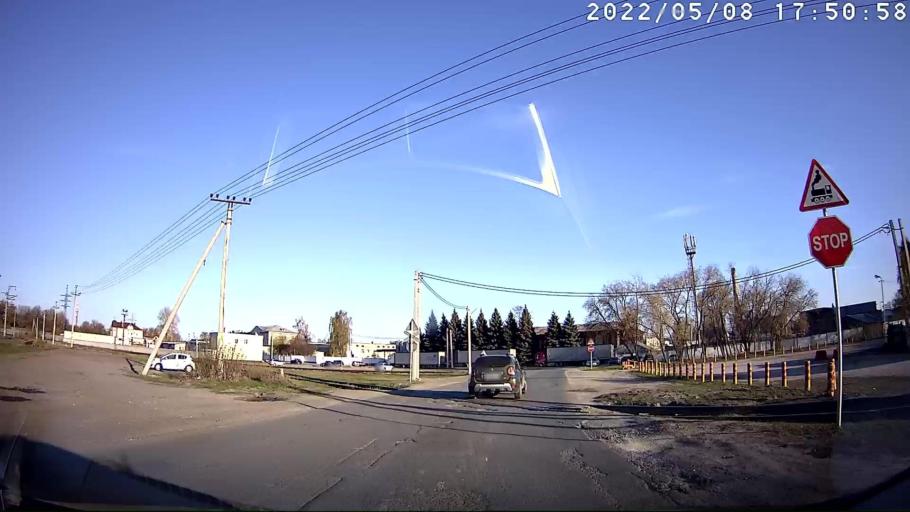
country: RU
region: Tatarstan
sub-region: Zelenodol'skiy Rayon
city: Zelenodolsk
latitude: 55.8421
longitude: 48.4923
